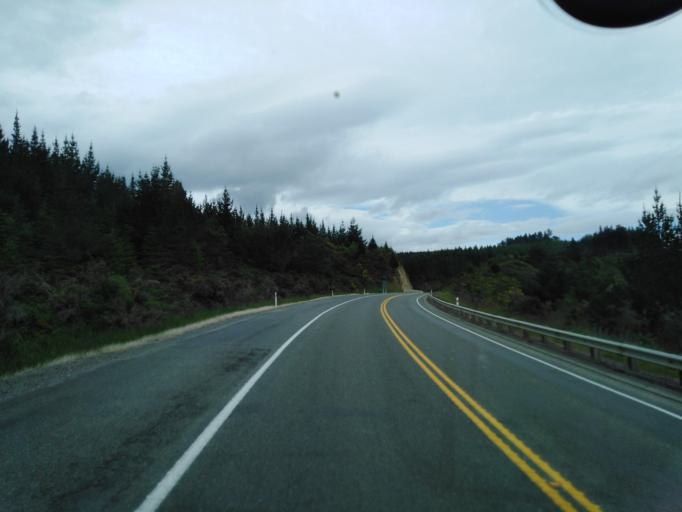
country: NZ
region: Tasman
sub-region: Tasman District
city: Wakefield
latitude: -41.4807
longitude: 172.9133
